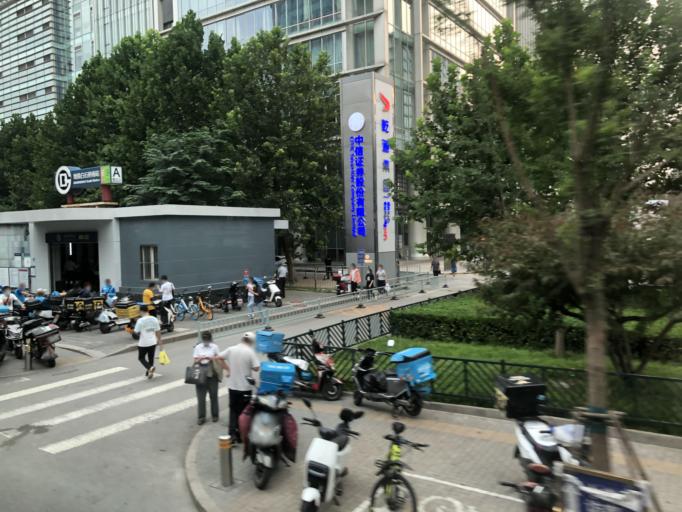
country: CN
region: Beijing
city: Jinrongjie
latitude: 39.9328
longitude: 116.3191
